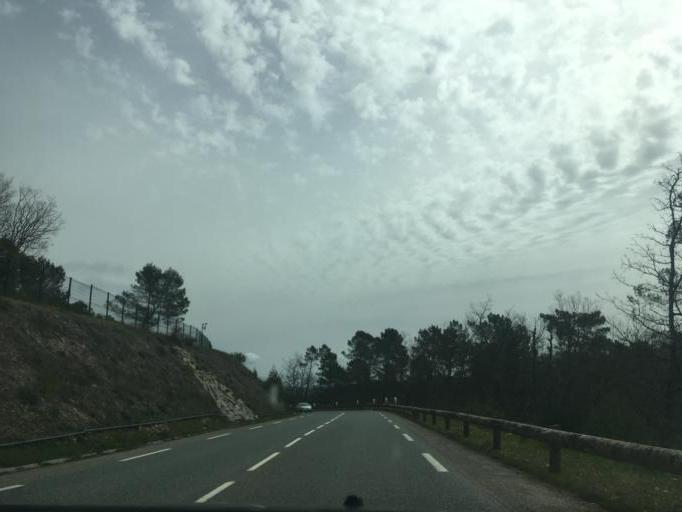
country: FR
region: Provence-Alpes-Cote d'Azur
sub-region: Departement du Var
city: Callian
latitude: 43.5904
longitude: 6.7337
